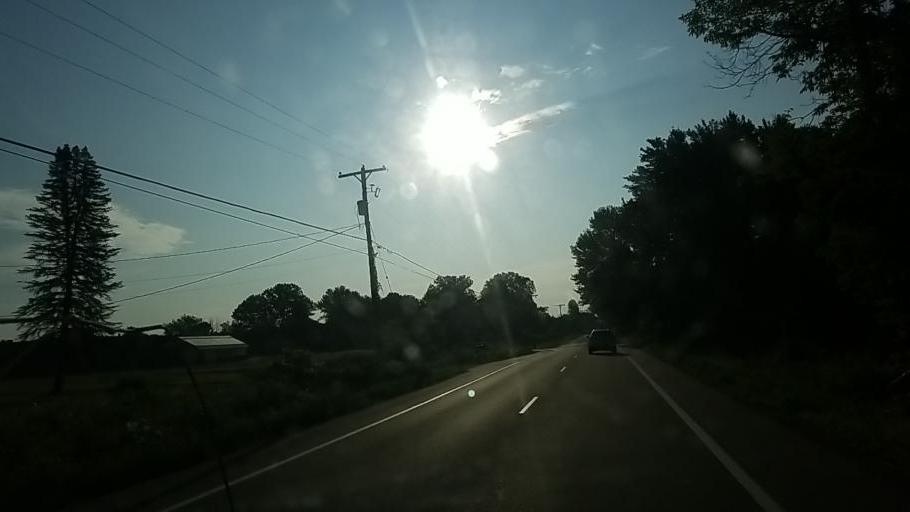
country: US
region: Michigan
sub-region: Montcalm County
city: Stanton
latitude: 43.2500
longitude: -85.1067
